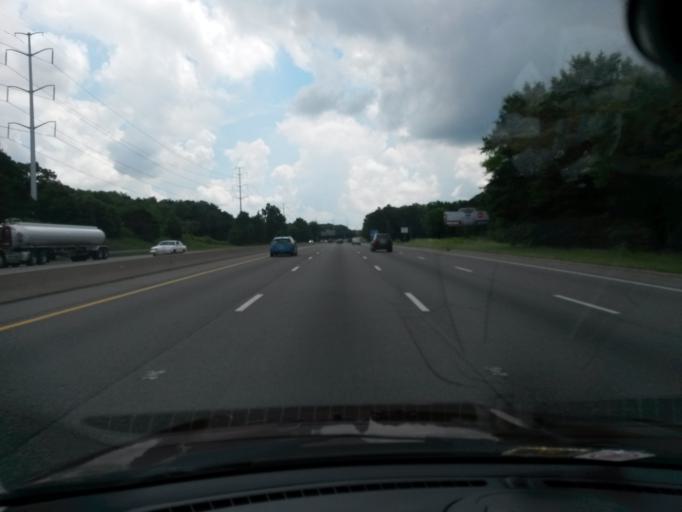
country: US
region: Virginia
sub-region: Chesterfield County
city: Bellwood
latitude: 37.4284
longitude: -77.4304
